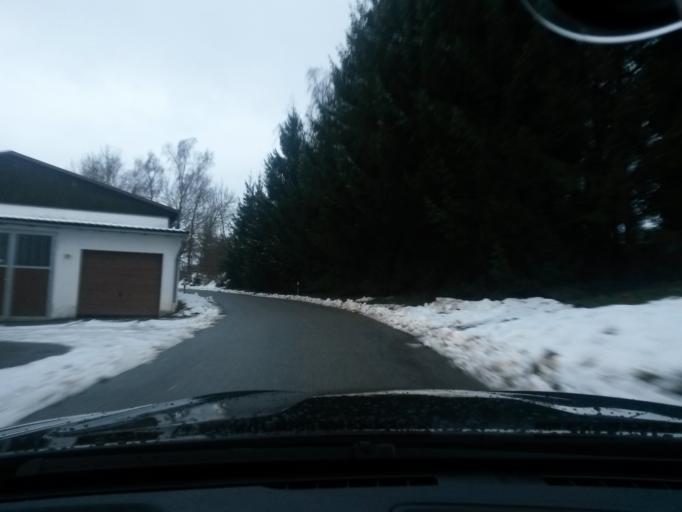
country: DE
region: Bavaria
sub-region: Lower Bavaria
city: Tiefenbach
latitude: 48.4736
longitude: 12.0885
